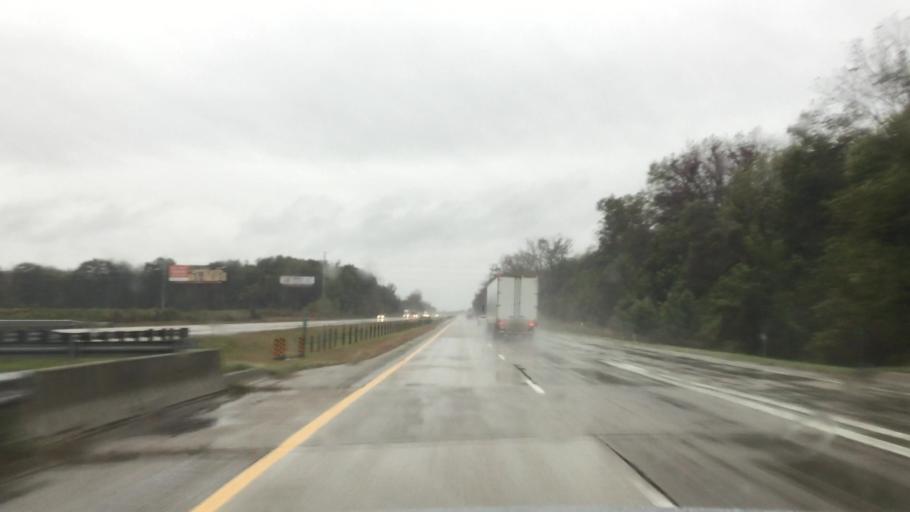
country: US
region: Michigan
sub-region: Van Buren County
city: Hartford
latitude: 42.1920
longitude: -86.1713
